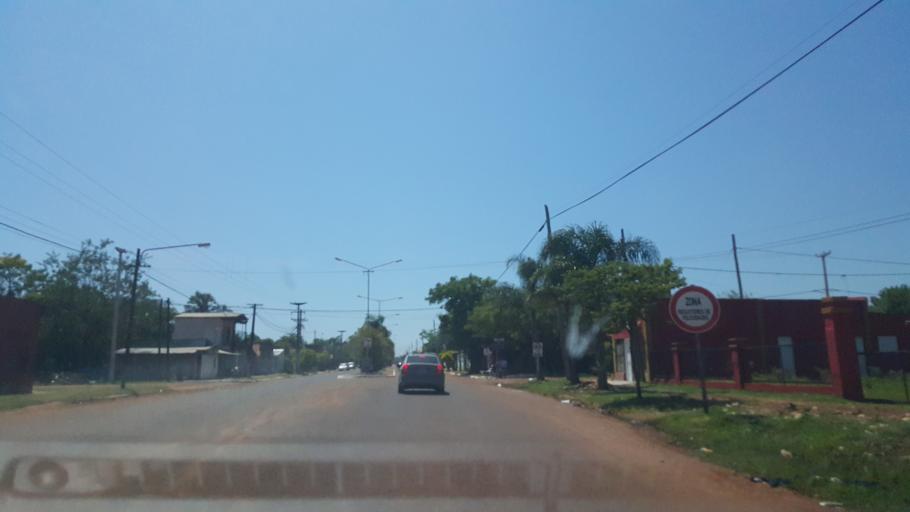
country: AR
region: Corrientes
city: Santo Tome
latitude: -28.5469
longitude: -56.0608
